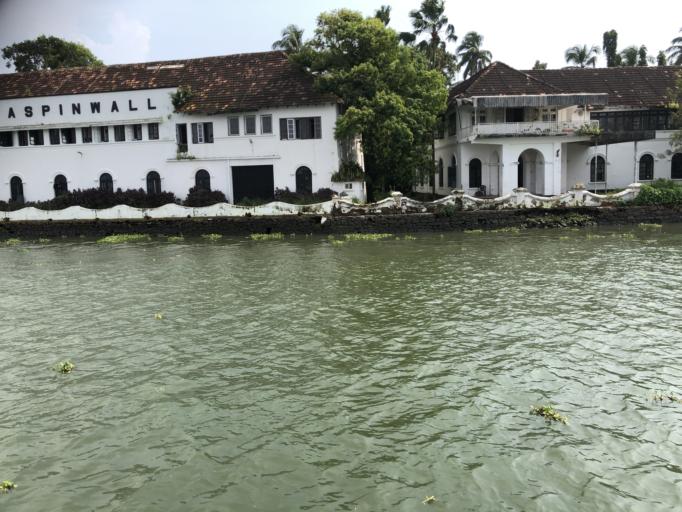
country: IN
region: Kerala
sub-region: Ernakulam
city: Cochin
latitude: 9.9694
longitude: 76.2463
